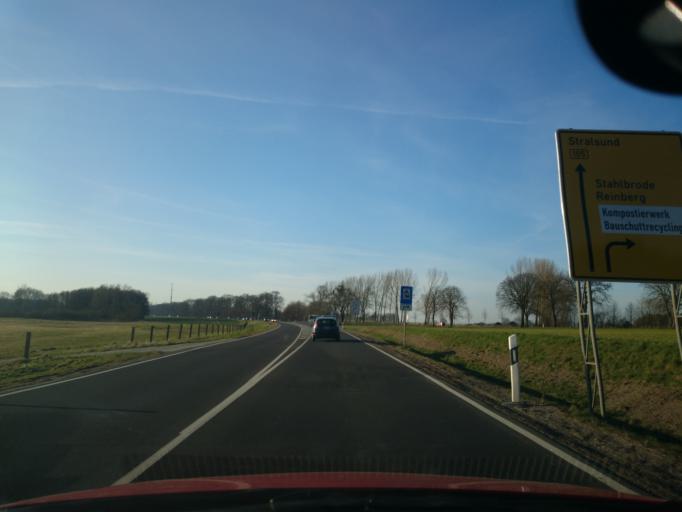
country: DE
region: Mecklenburg-Vorpommern
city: Brandshagen
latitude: 54.2146
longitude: 13.2448
